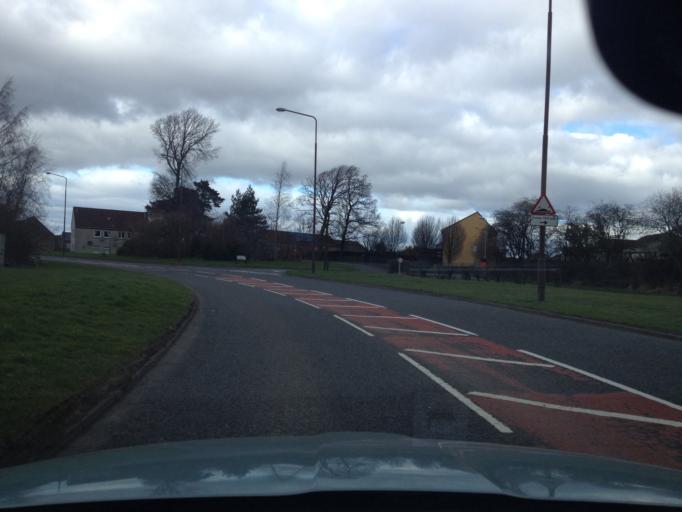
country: GB
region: Scotland
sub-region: West Lothian
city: Mid Calder
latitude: 55.8766
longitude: -3.4947
